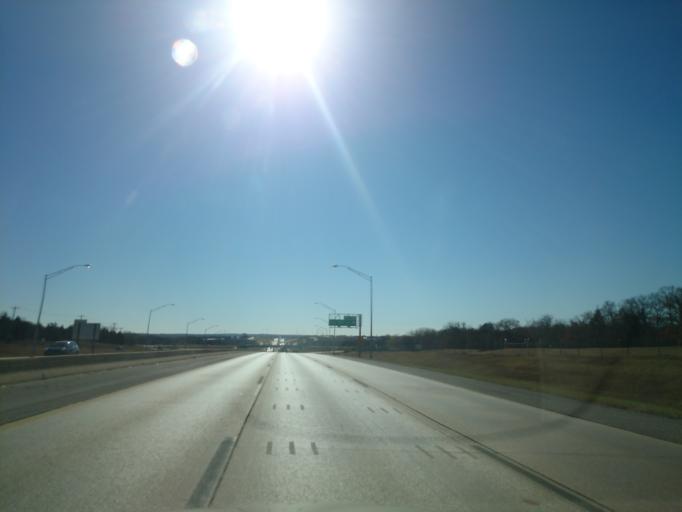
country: US
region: Oklahoma
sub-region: Oklahoma County
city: Edmond
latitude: 35.6291
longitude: -97.4250
